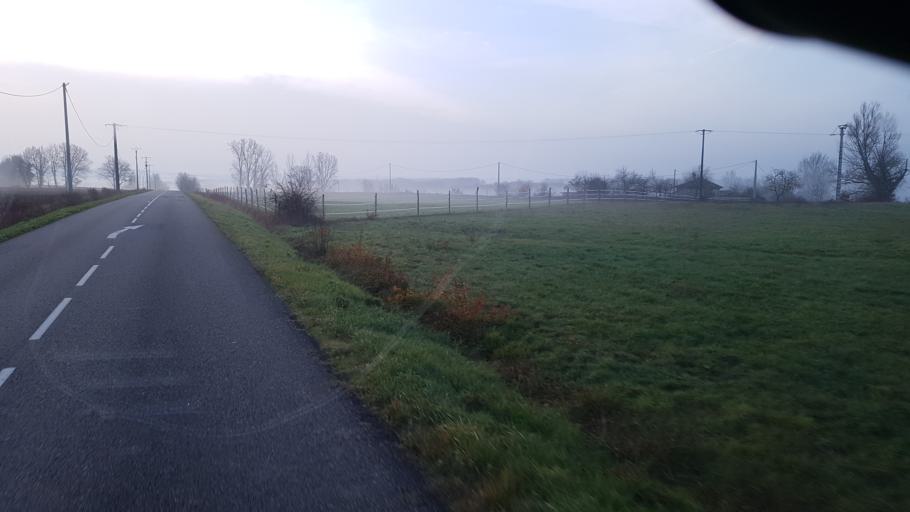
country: FR
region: Midi-Pyrenees
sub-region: Departement du Tarn-et-Garonne
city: Monteils
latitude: 44.1310
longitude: 1.5805
